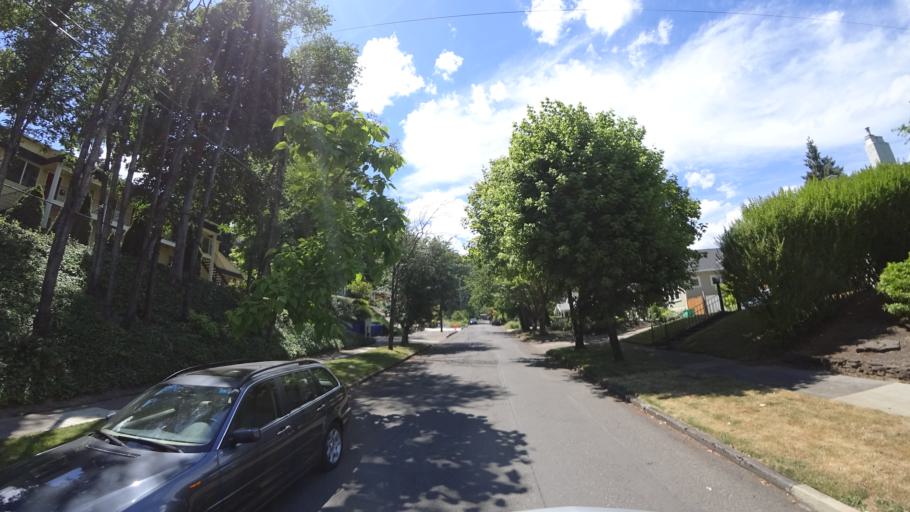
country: US
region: Oregon
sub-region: Multnomah County
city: Portland
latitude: 45.5374
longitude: -122.7125
